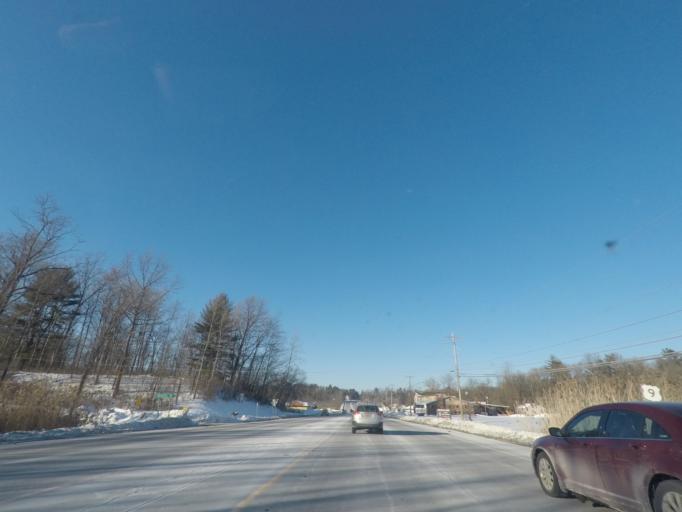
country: US
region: New York
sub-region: Saratoga County
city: Saratoga Springs
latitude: 43.0363
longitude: -73.7897
